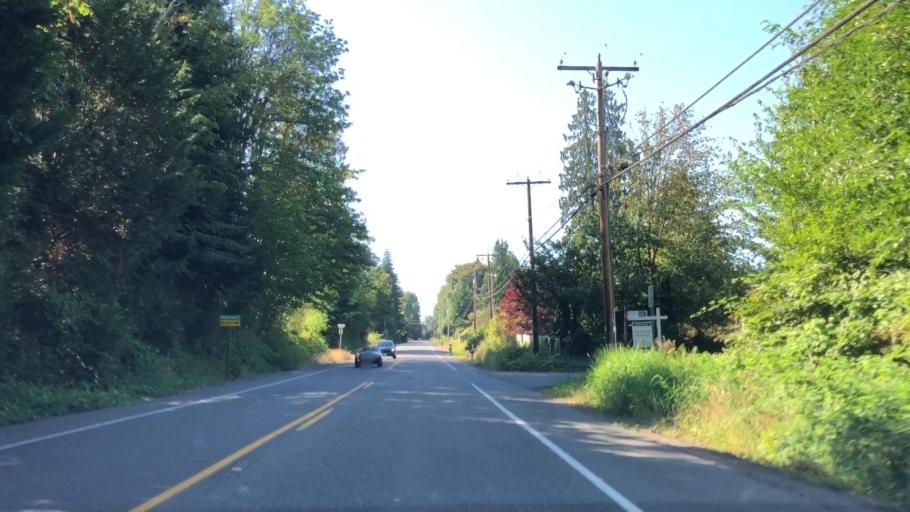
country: US
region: Washington
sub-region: Kitsap County
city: Kingston
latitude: 47.7879
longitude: -122.5038
